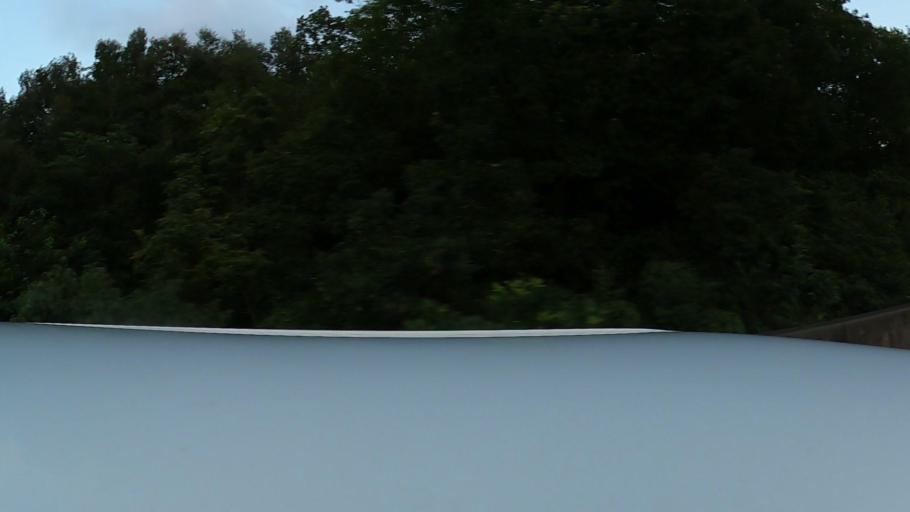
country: JP
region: Miyazaki
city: Nobeoka
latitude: 32.4574
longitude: 131.6143
